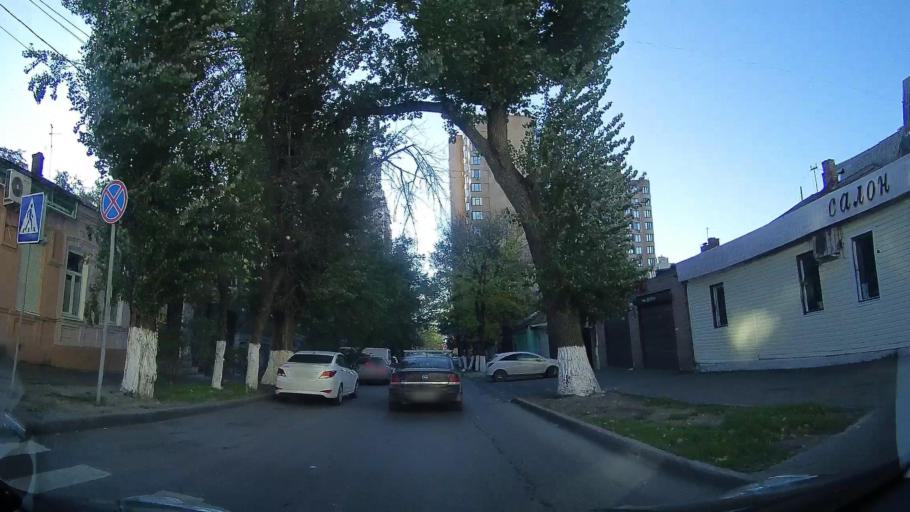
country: RU
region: Rostov
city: Rostov-na-Donu
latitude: 47.2236
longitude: 39.7005
